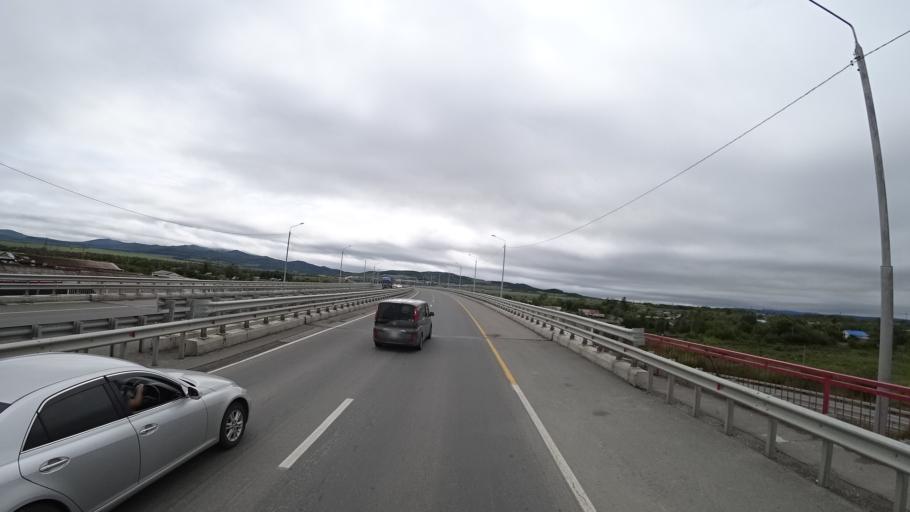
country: RU
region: Primorskiy
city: Monastyrishche
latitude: 44.1933
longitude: 132.4426
